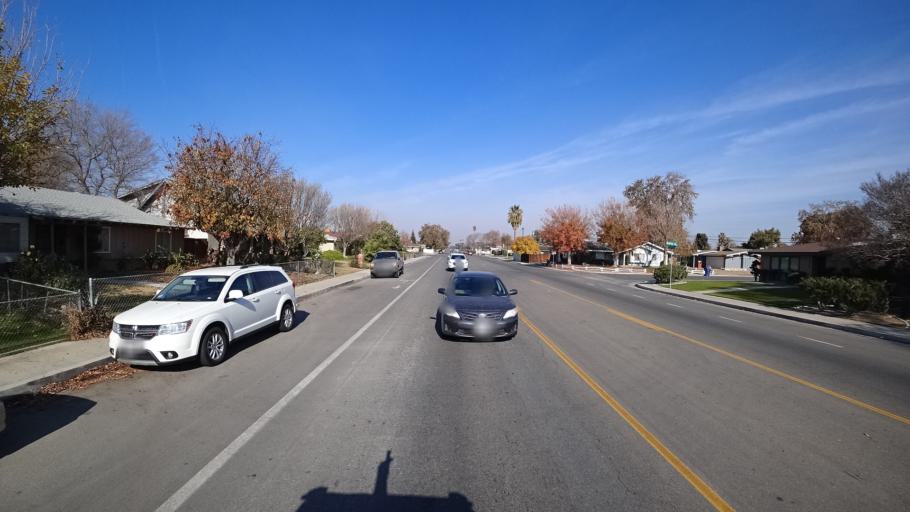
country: US
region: California
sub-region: Kern County
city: Bakersfield
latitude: 35.3270
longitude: -119.0301
